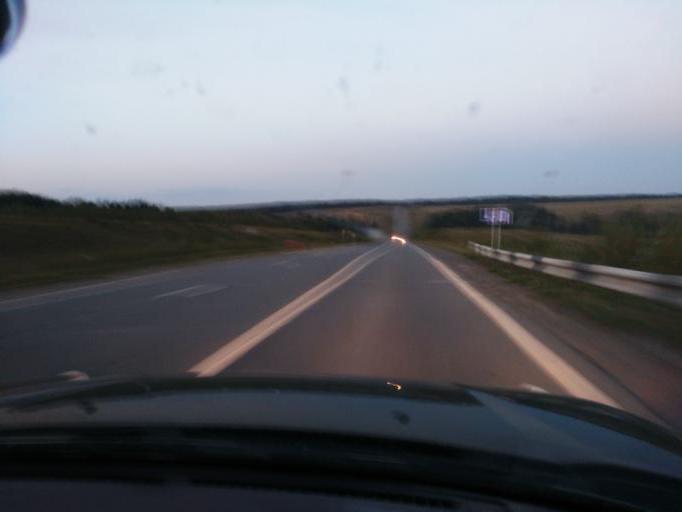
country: RU
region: Perm
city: Verkhnechusovskiye Gorodki
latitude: 58.2213
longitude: 57.1748
